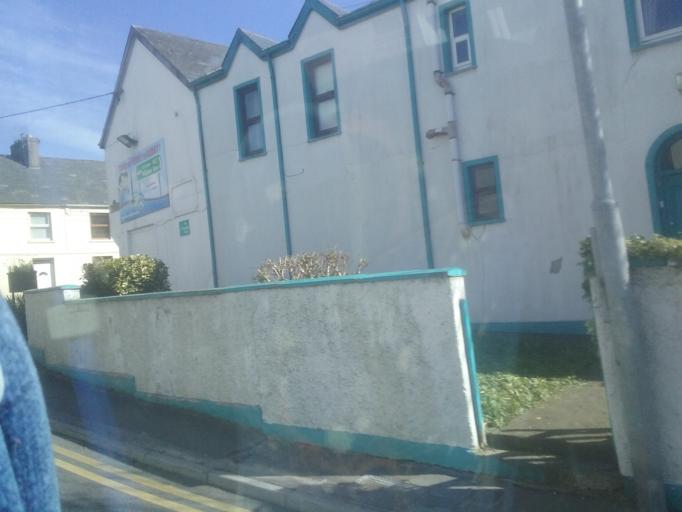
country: IE
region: Munster
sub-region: An Clar
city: Kilrush
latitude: 52.6374
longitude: -9.4817
